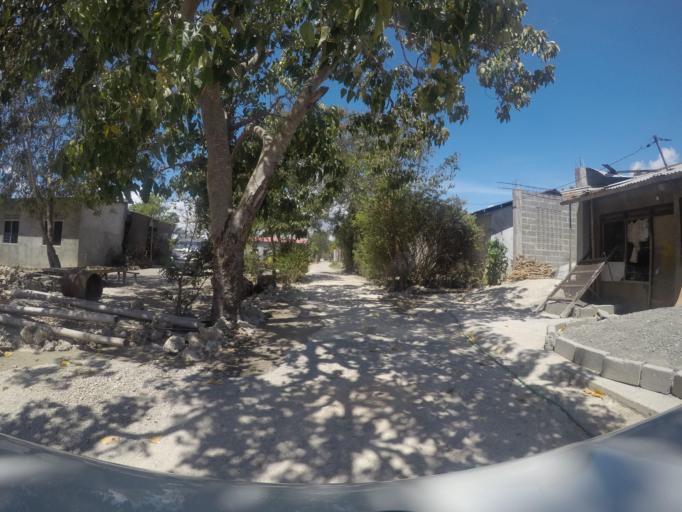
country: TL
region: Baucau
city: Baucau
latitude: -8.4829
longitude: 126.4512
